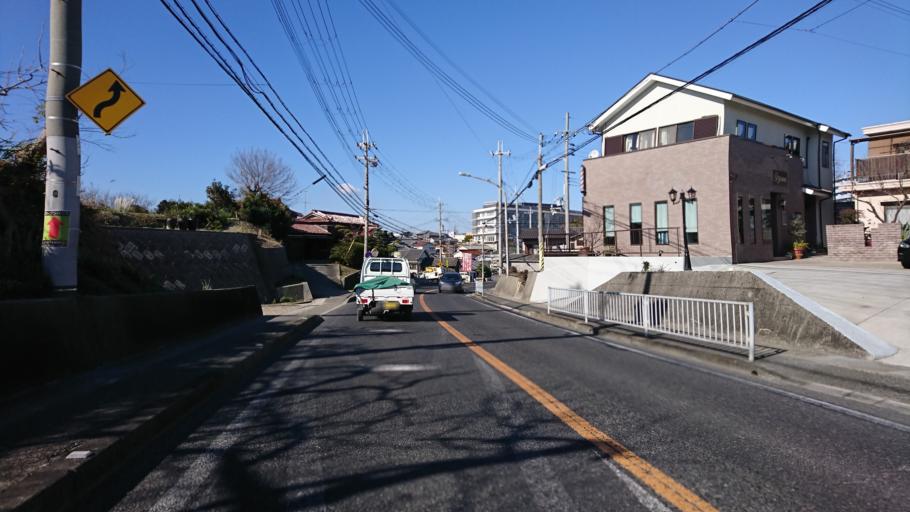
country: JP
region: Hyogo
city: Akashi
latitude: 34.6588
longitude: 134.9524
